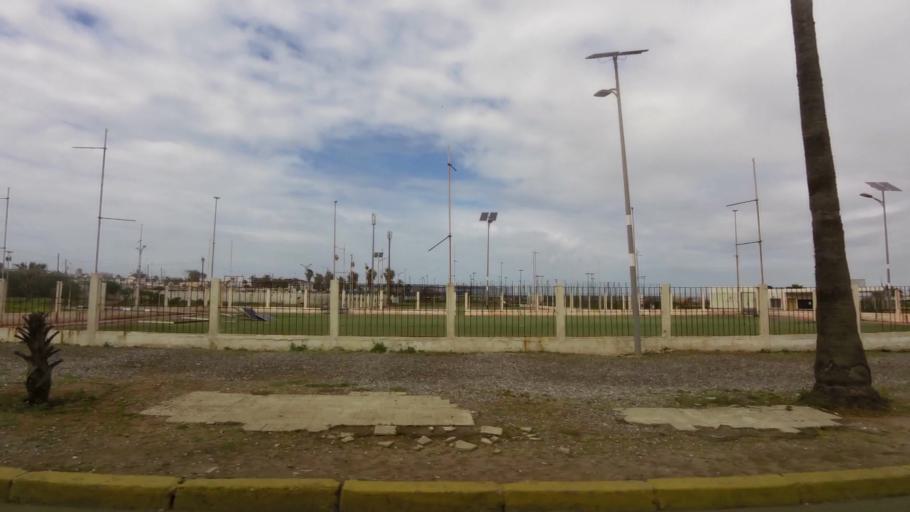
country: MA
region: Grand Casablanca
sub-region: Casablanca
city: Casablanca
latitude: 33.6068
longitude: -7.6512
